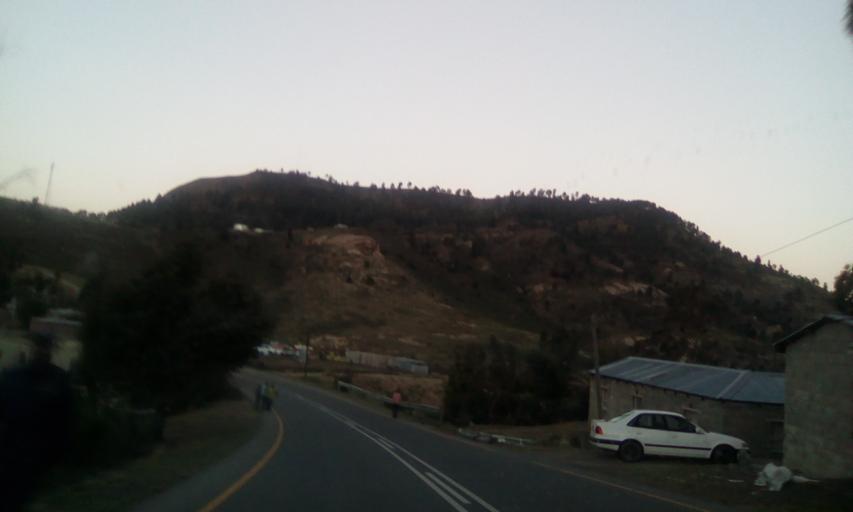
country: LS
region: Qacha's Nek
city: Qacha's Nek
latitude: -30.1282
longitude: 28.6880
